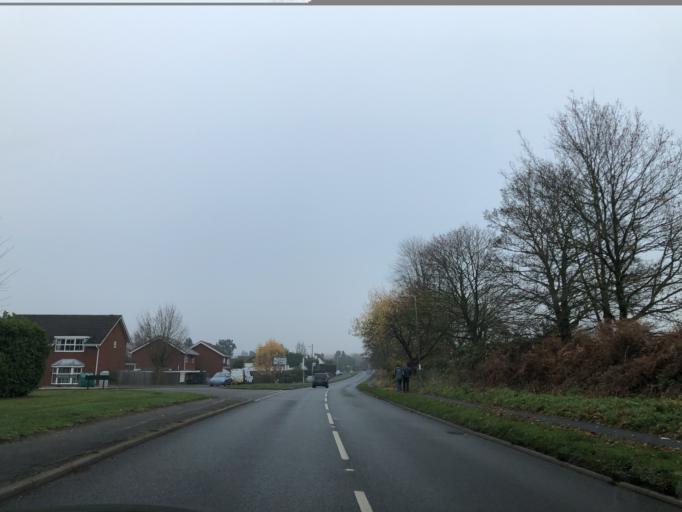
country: GB
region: England
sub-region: Solihull
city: Balsall Common
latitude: 52.3877
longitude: -1.6638
